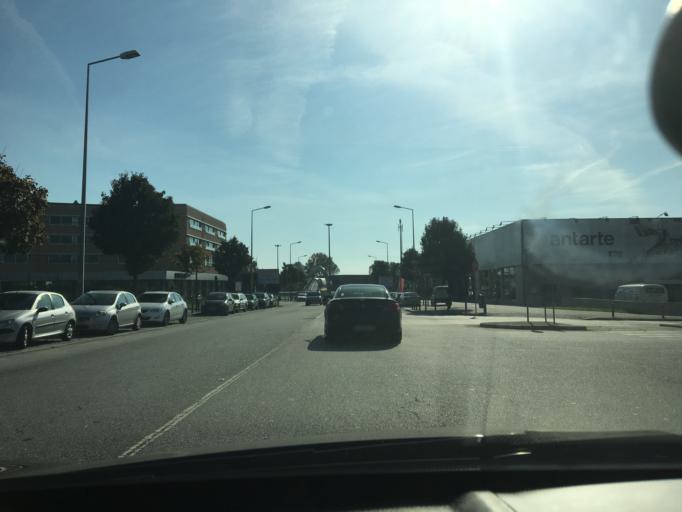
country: PT
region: Porto
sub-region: Matosinhos
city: Leca da Palmeira
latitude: 41.2036
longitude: -8.6929
